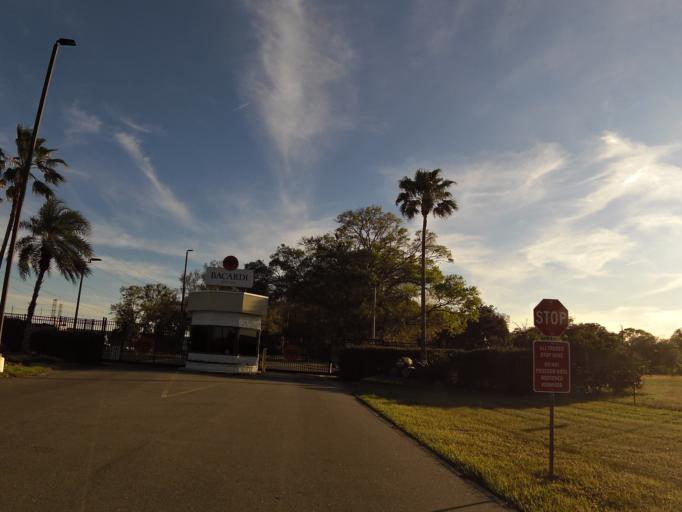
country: US
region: Florida
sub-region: Duval County
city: Jacksonville
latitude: 30.4604
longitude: -81.6358
